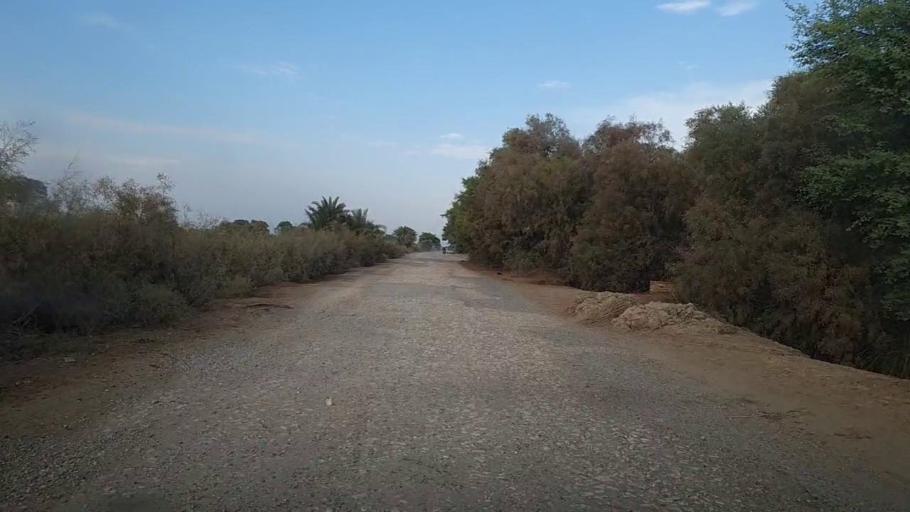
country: PK
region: Sindh
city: Thul
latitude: 28.2912
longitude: 68.8735
